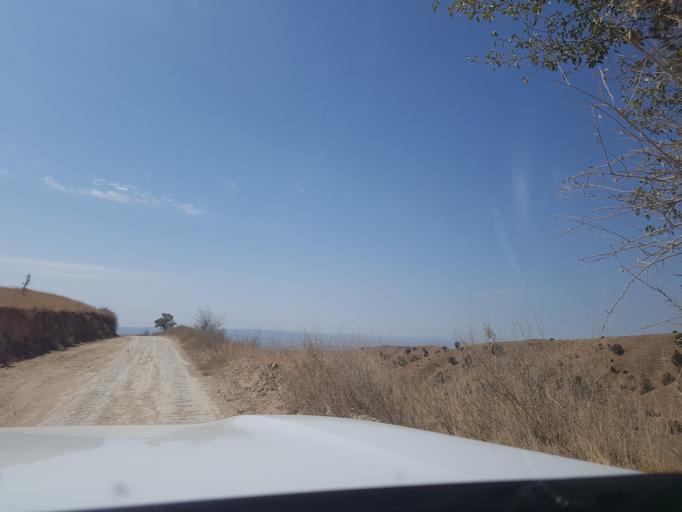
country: TM
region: Ahal
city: Baharly
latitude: 38.2955
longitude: 56.9354
